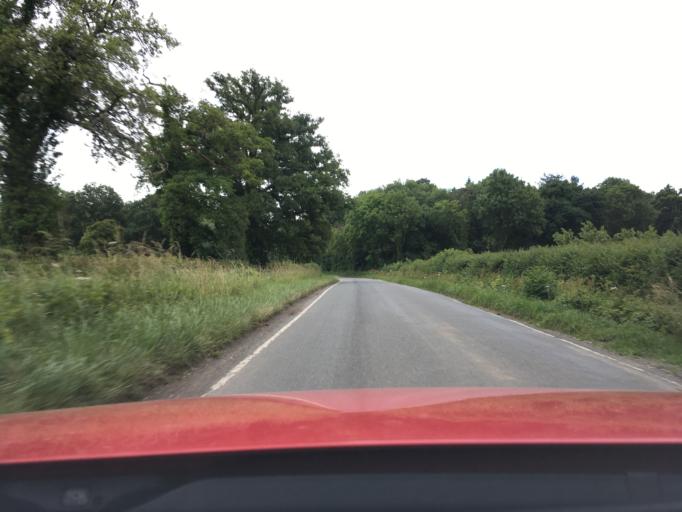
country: GB
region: England
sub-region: Gloucestershire
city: Dursley
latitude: 51.7833
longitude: -2.3935
